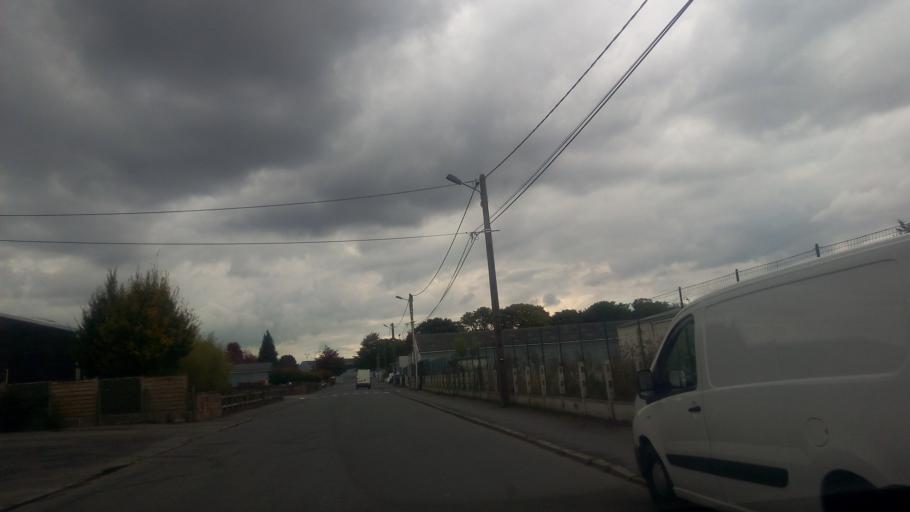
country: FR
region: Brittany
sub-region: Departement d'Ille-et-Vilaine
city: Redon
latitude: 47.6651
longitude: -2.0761
